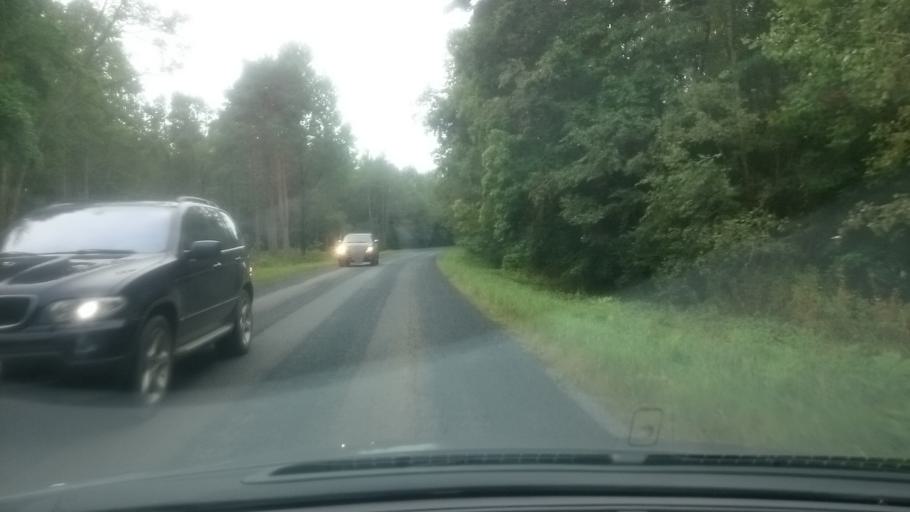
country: EE
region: Harju
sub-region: Raasiku vald
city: Raasiku
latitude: 59.4729
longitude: 25.2478
